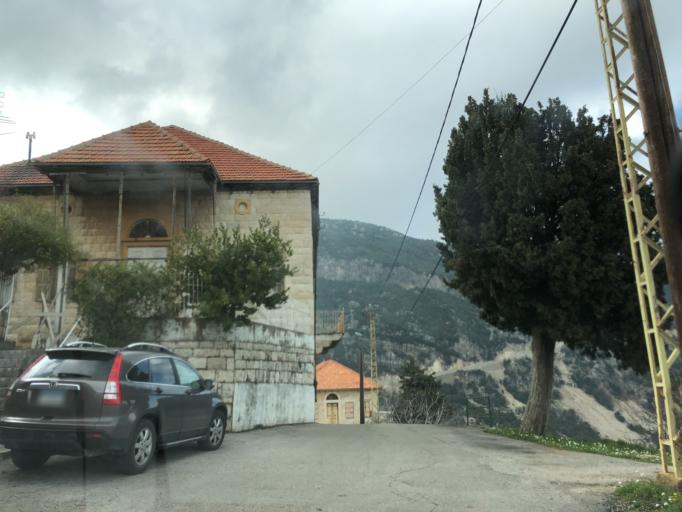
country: LB
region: Liban-Nord
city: Amioun
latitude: 34.2069
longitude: 35.8383
